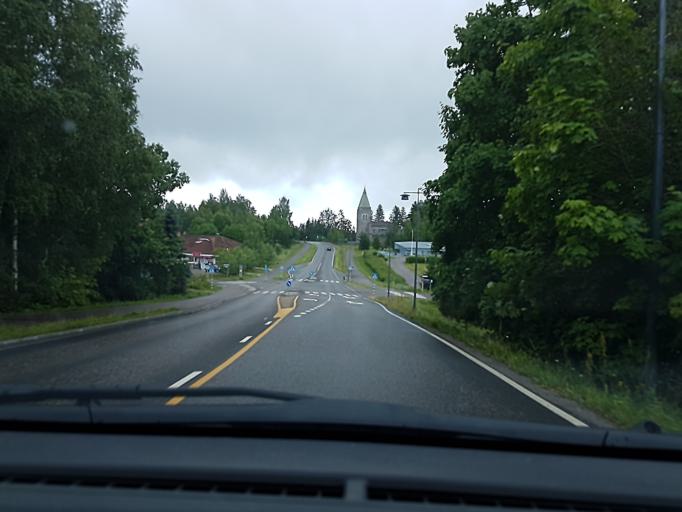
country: FI
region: Uusimaa
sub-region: Helsinki
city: Pornainen
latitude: 60.4765
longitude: 25.3744
